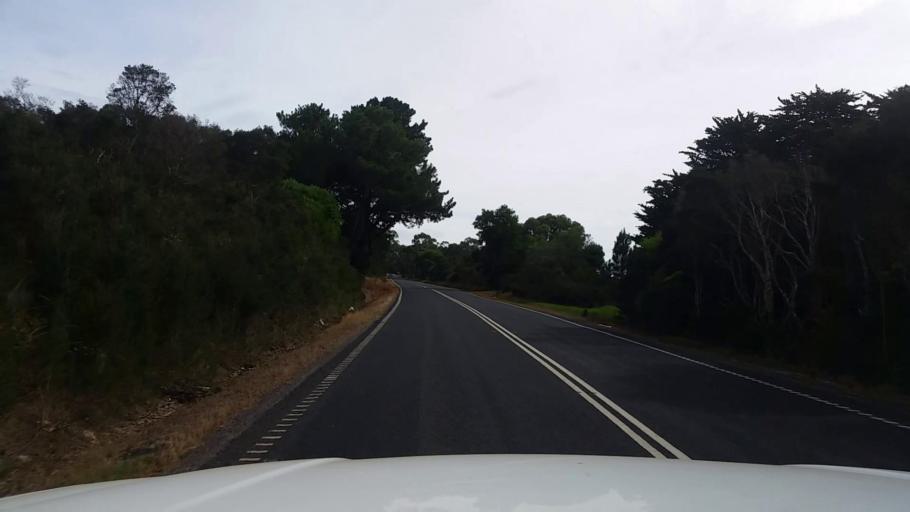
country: AU
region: Victoria
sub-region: Mornington Peninsula
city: Merricks
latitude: -38.3168
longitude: 145.0885
